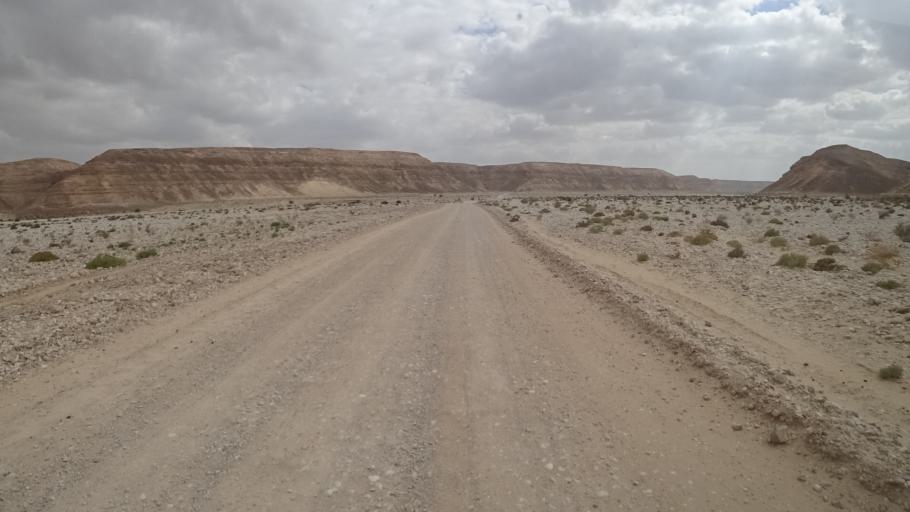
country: YE
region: Al Mahrah
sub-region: Shahan
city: Shihan as Sufla
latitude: 17.4683
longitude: 53.0047
